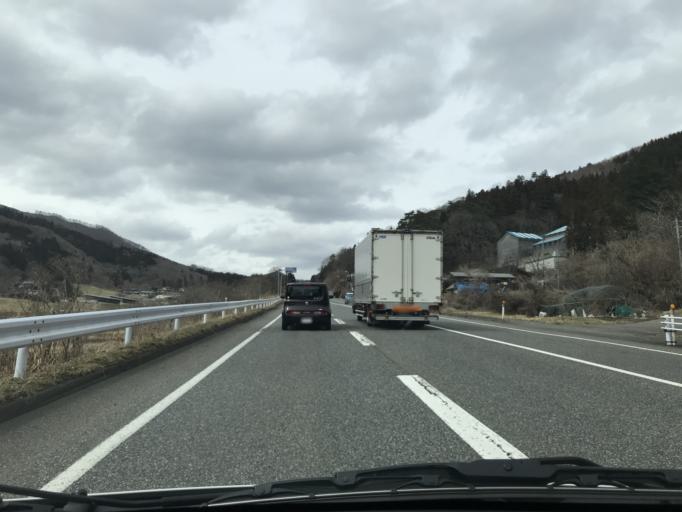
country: JP
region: Iwate
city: Tono
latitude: 39.3388
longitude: 141.4427
